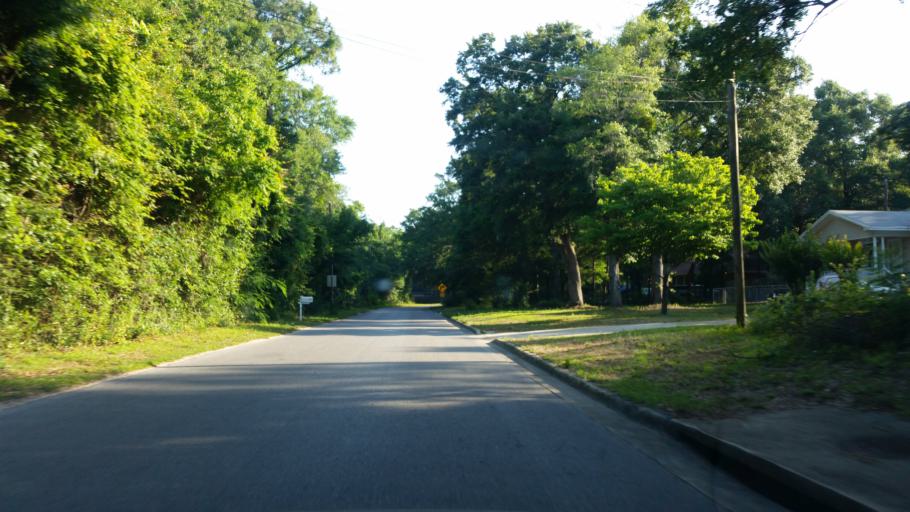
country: US
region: Florida
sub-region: Escambia County
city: Ferry Pass
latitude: 30.5361
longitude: -87.2161
